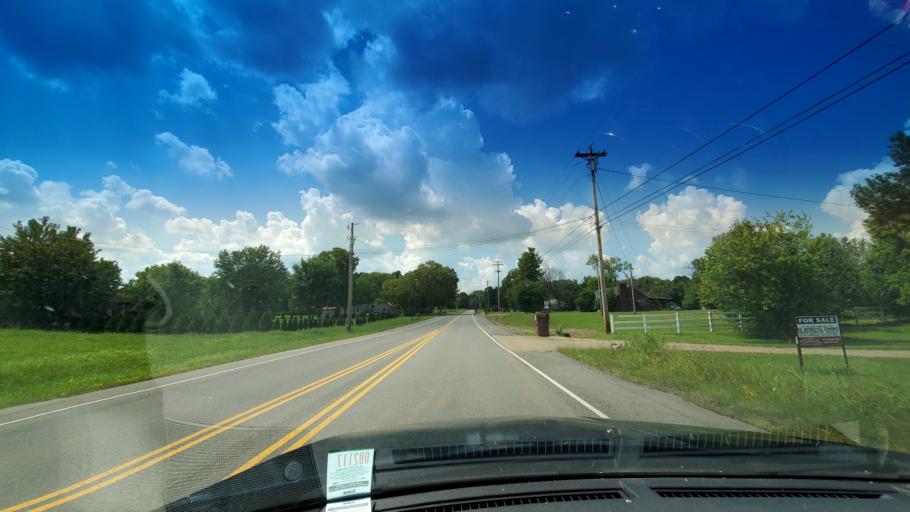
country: US
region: Tennessee
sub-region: Wilson County
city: Lebanon
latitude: 36.1804
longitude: -86.3290
